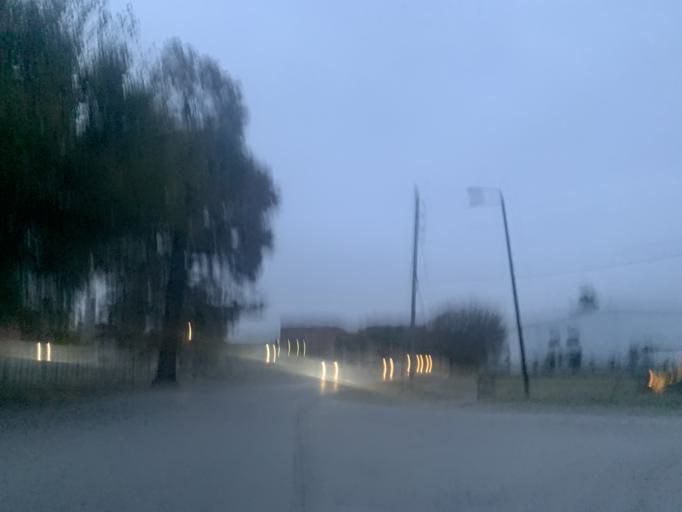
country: US
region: Kentucky
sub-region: Jefferson County
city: Shively
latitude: 38.2160
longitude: -85.7886
